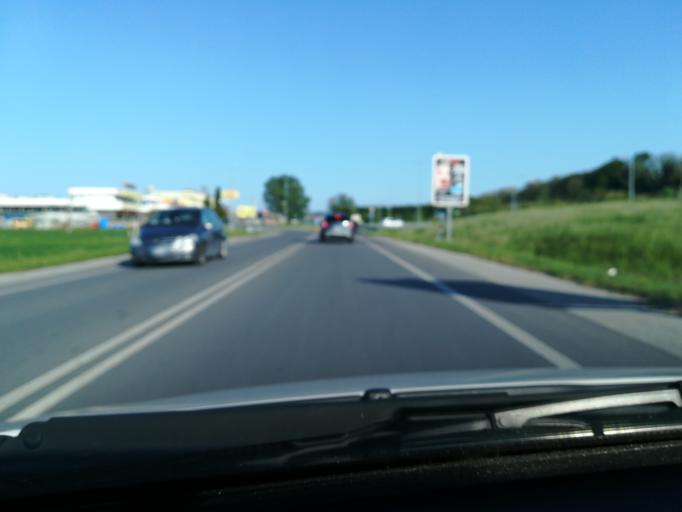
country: IT
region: Emilia-Romagna
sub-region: Provincia di Rimini
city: Misano Adriatico
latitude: 43.9715
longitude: 12.7009
